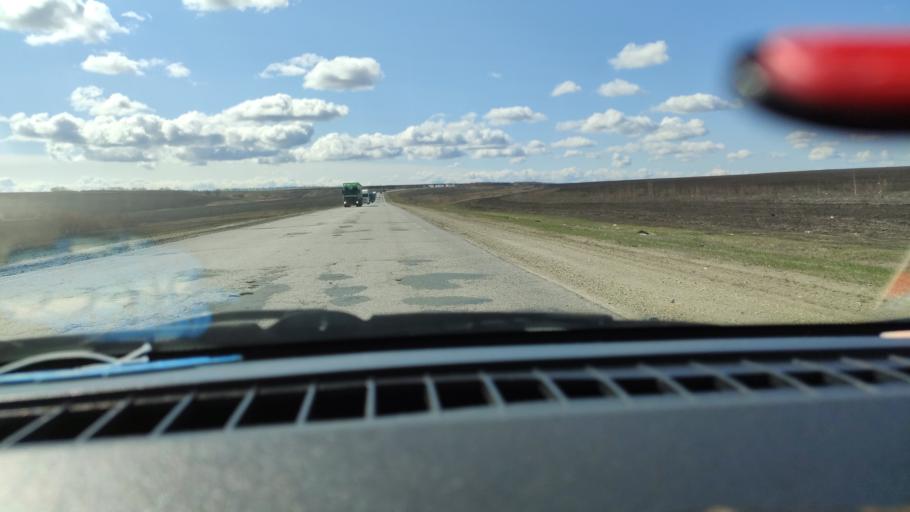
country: RU
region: Samara
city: Varlamovo
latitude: 53.0092
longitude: 48.3322
